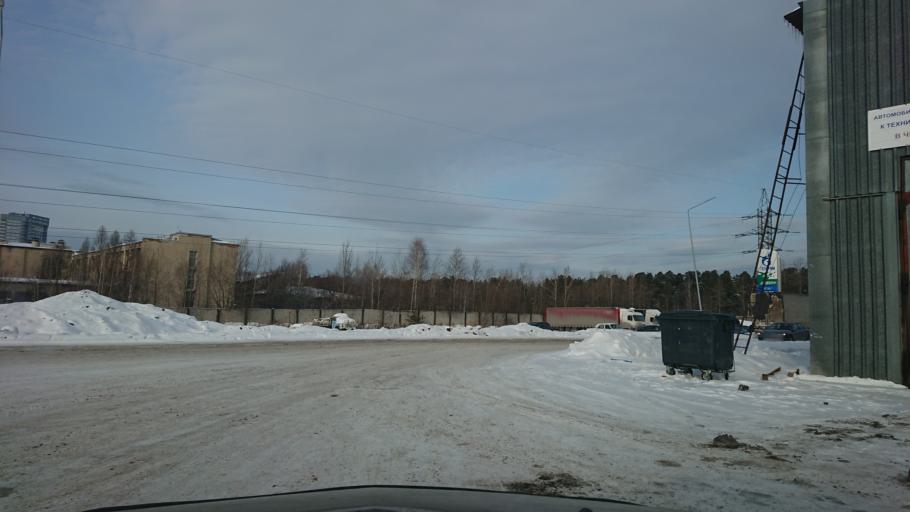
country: RU
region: Sverdlovsk
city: Sovkhoznyy
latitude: 56.7777
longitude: 60.5608
